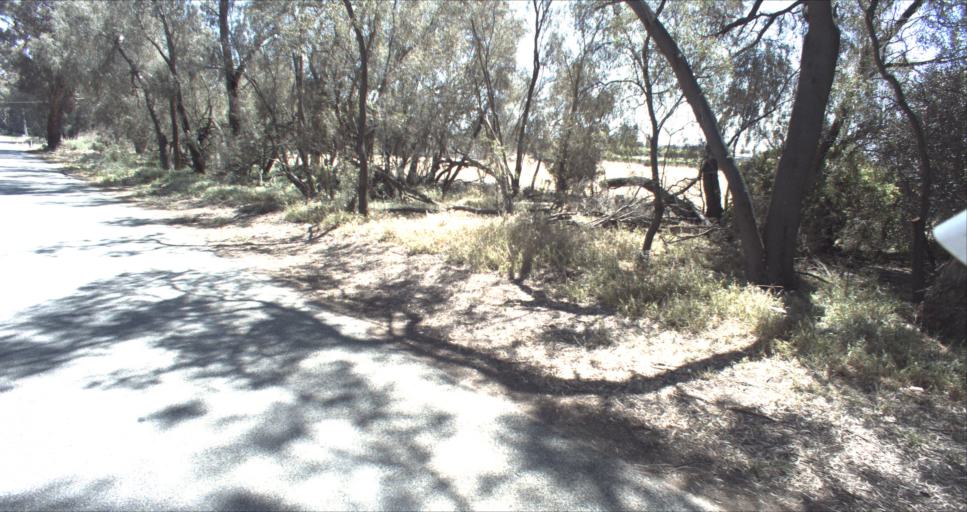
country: AU
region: New South Wales
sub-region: Leeton
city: Leeton
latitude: -34.5319
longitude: 146.3392
